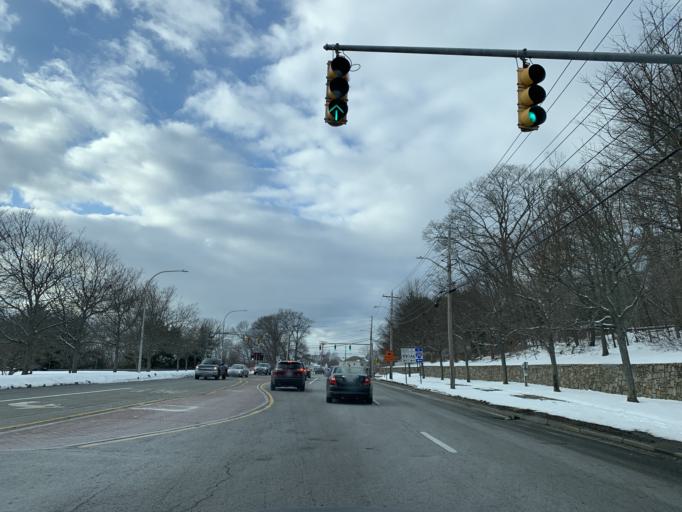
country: US
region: Rhode Island
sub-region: Providence County
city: Cumberland Hill
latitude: 41.9860
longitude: -71.4799
